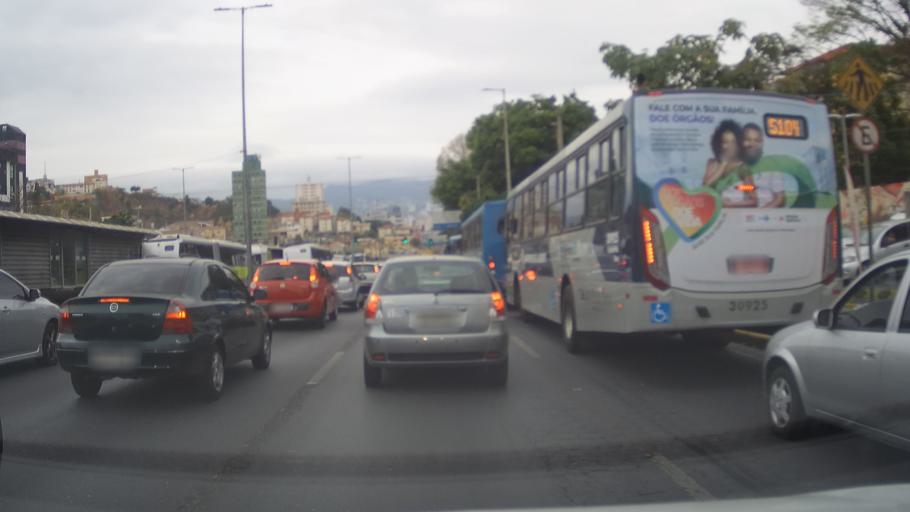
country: BR
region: Minas Gerais
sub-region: Belo Horizonte
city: Belo Horizonte
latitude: -19.9002
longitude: -43.9464
